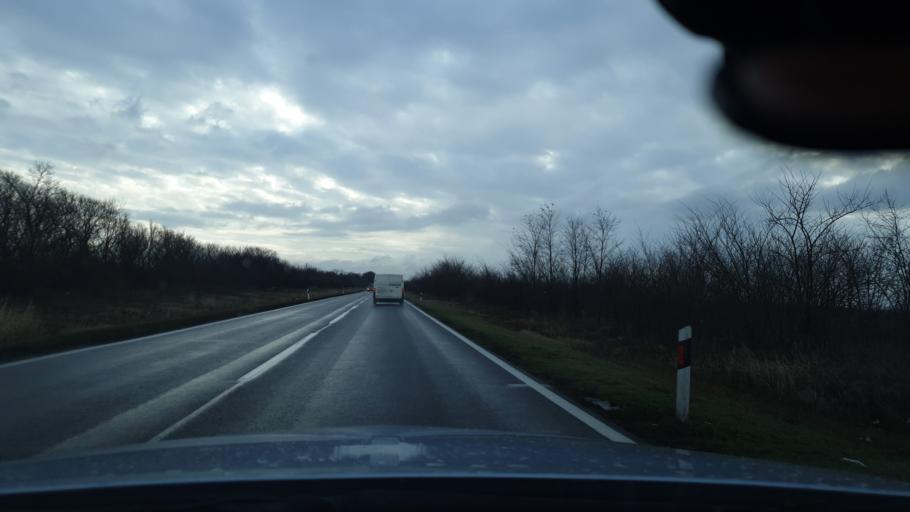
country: RS
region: Autonomna Pokrajina Vojvodina
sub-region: Juznobanatski Okrug
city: Kovin
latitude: 44.7646
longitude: 20.9529
